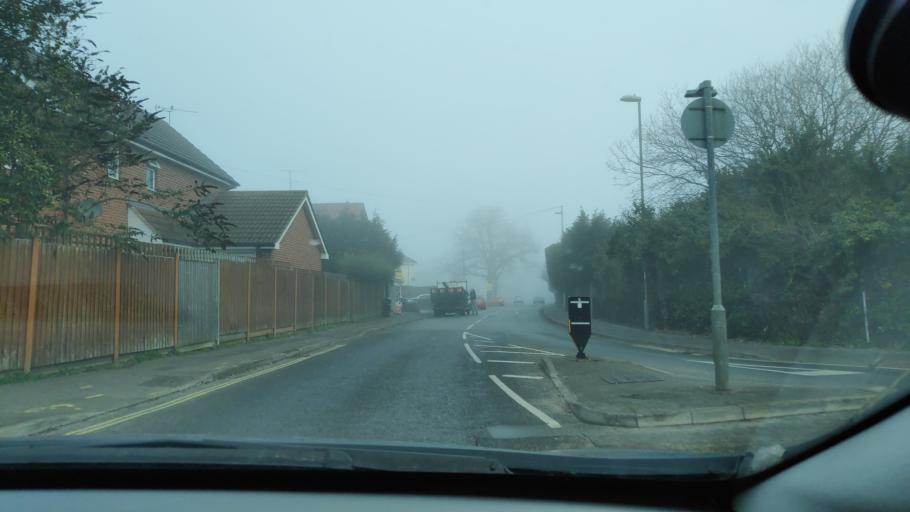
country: GB
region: England
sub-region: Hampshire
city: Farnborough
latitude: 51.2818
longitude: -0.7383
